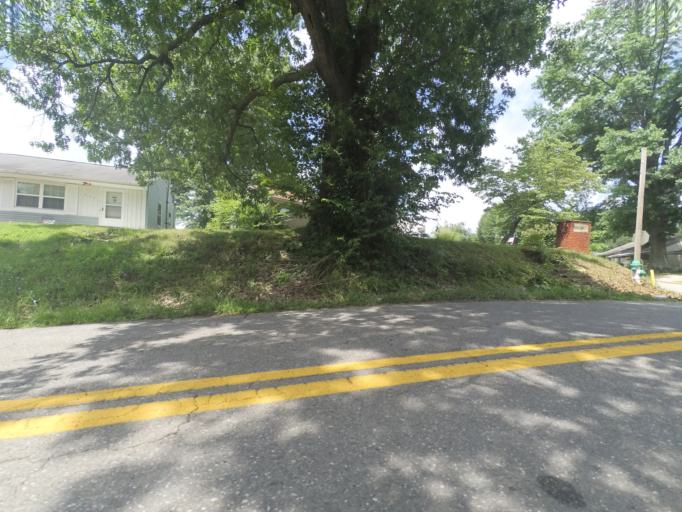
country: US
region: West Virginia
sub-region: Cabell County
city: Pea Ridge
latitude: 38.4030
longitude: -82.3829
